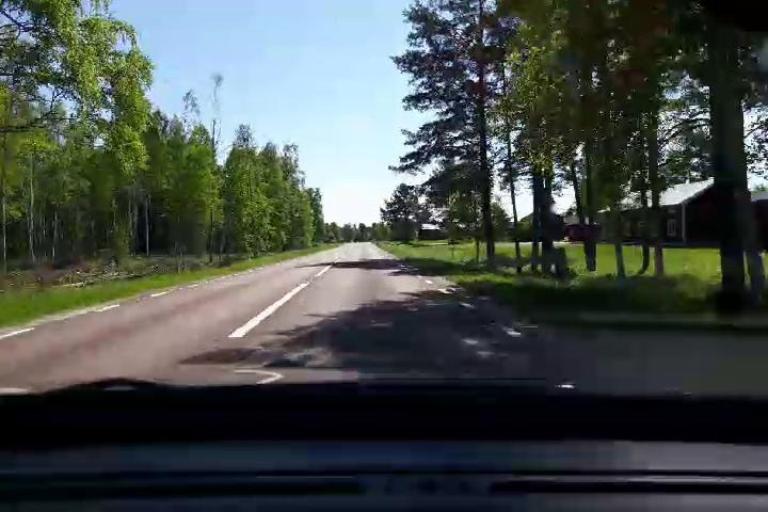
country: SE
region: Jaemtland
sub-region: Harjedalens Kommun
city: Sveg
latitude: 62.1608
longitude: 14.9506
